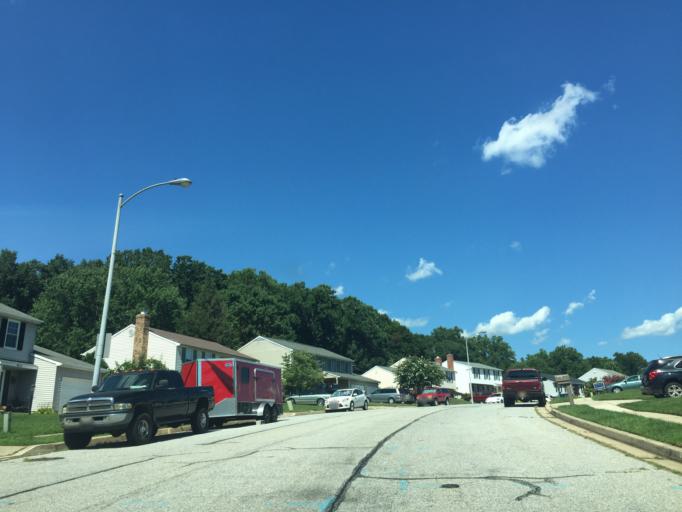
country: US
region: Maryland
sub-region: Baltimore County
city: Perry Hall
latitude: 39.4181
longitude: -76.4918
